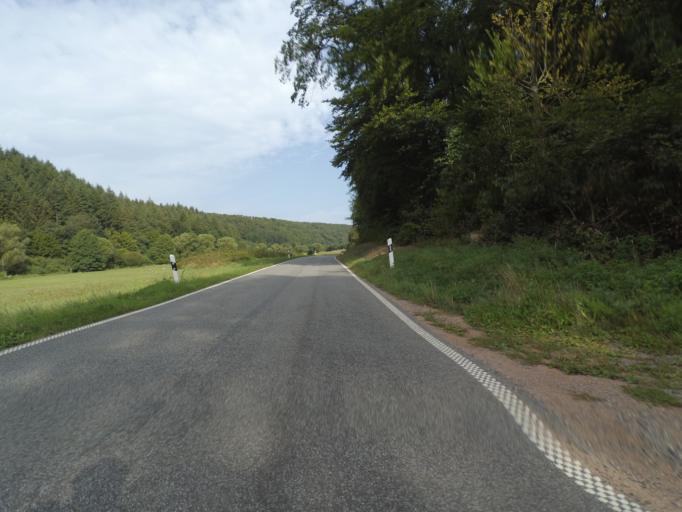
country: DE
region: Rheinland-Pfalz
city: Mannebach
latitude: 49.6493
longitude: 6.5105
